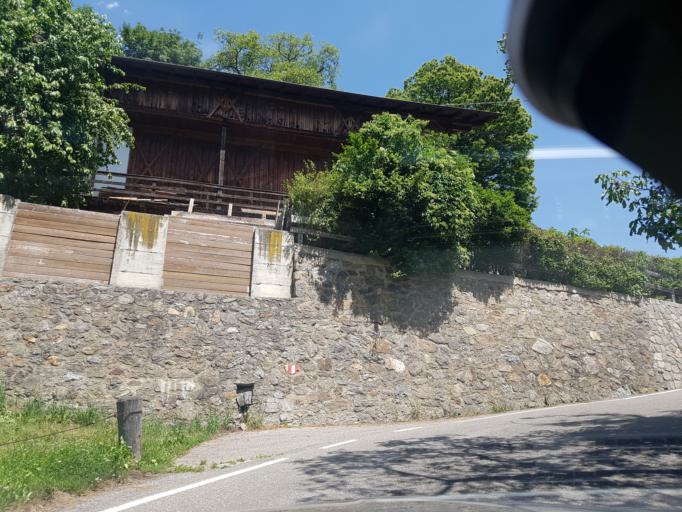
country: IT
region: Trentino-Alto Adige
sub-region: Bolzano
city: Villandro - Villanders
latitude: 46.6234
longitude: 11.5264
